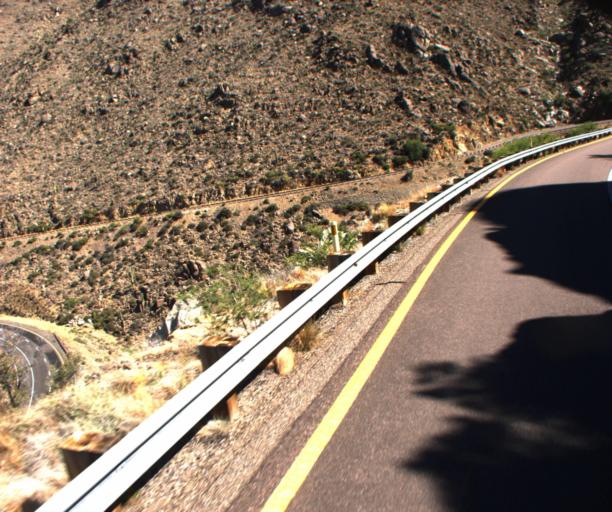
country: US
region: Arizona
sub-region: Yavapai County
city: Congress
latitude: 34.2040
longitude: -112.7816
